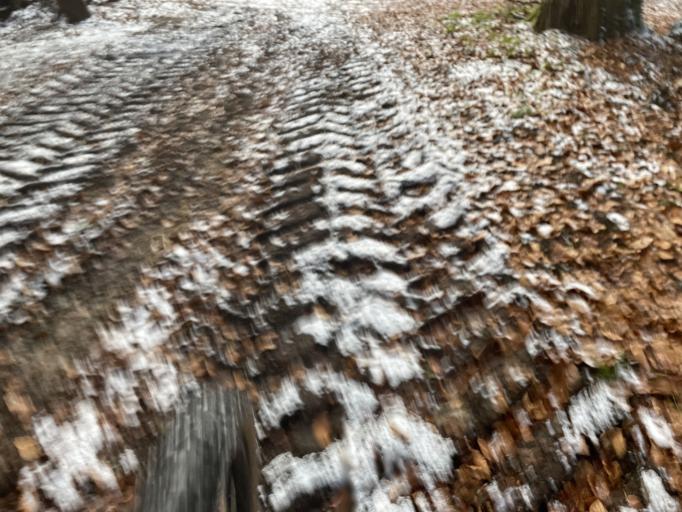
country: CH
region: Lucerne
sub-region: Entlebuch District
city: Oberdiessbach
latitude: 46.8507
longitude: 7.6096
